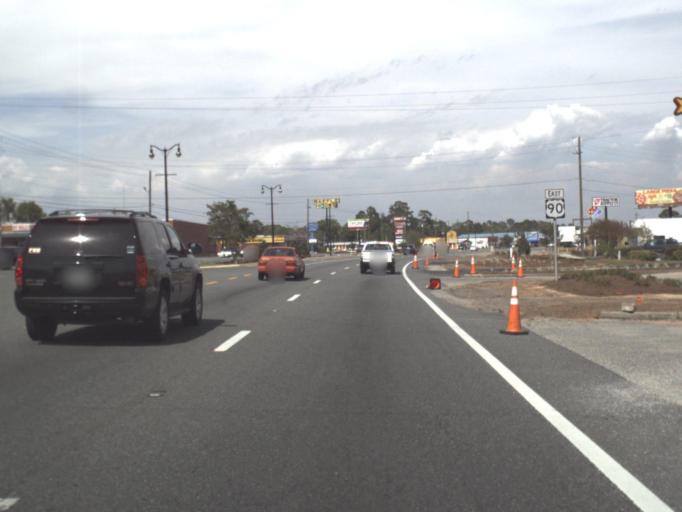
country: US
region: Florida
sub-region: Santa Rosa County
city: Milton
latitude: 30.6178
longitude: -87.0510
